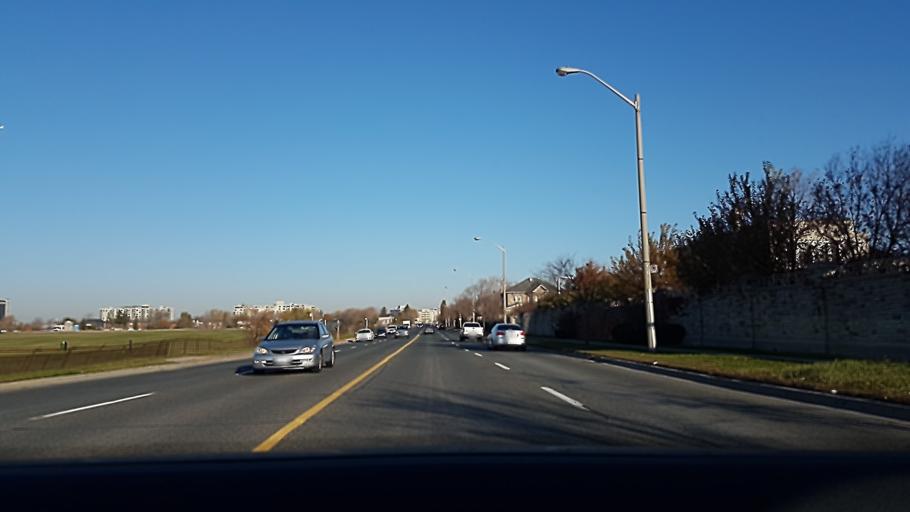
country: CA
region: Ontario
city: North York
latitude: 43.7437
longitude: -79.4528
